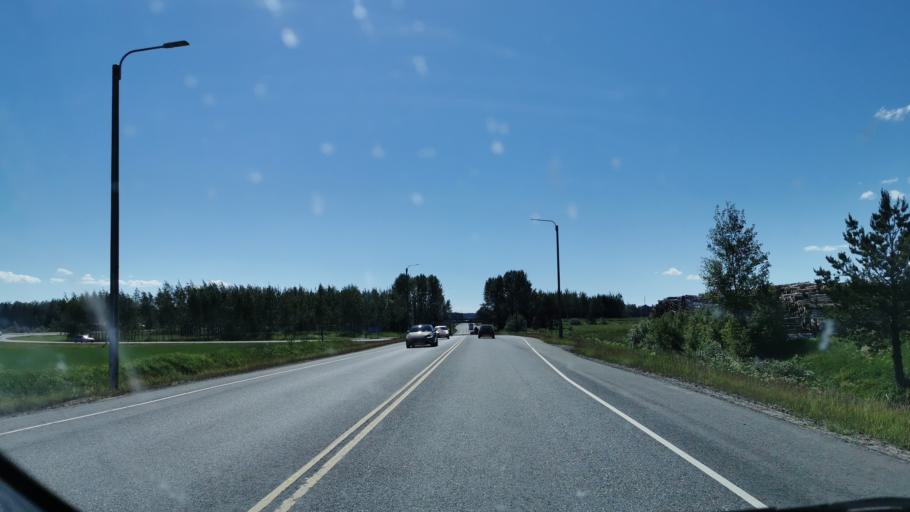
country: FI
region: Haeme
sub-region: Forssa
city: Humppila
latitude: 60.9548
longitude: 23.3444
